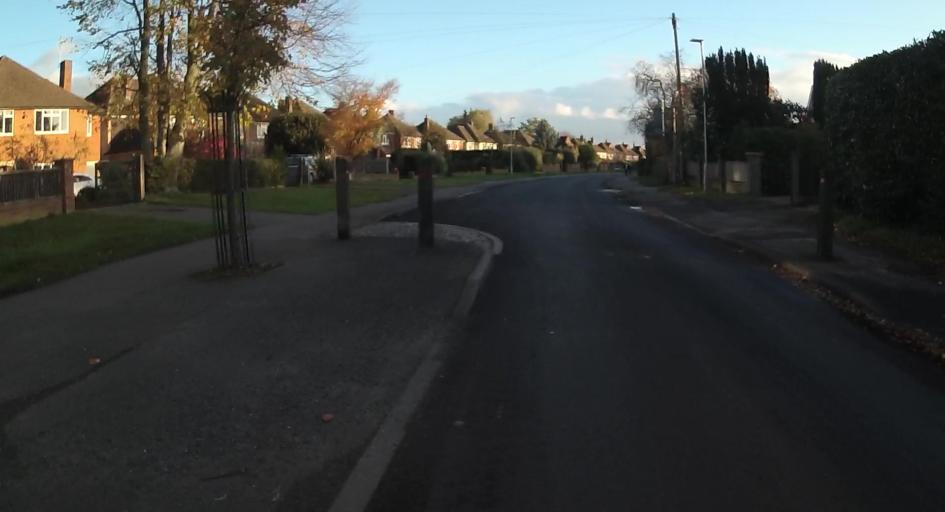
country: GB
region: England
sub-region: Wokingham
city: Wokingham
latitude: 51.4094
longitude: -0.8189
